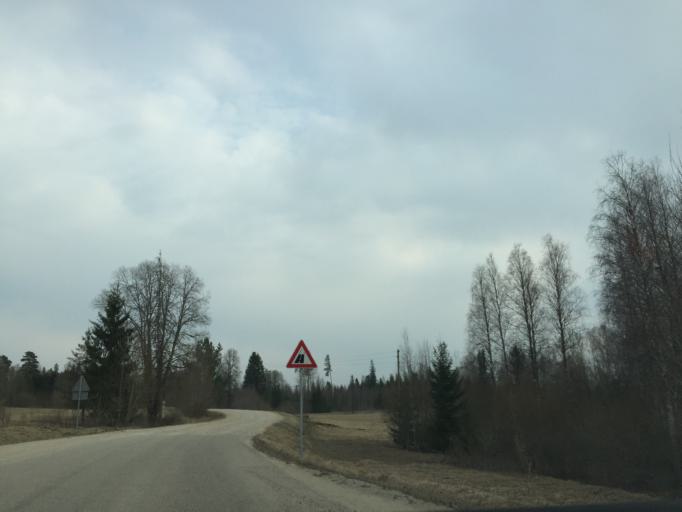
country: LV
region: Priekuli
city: Priekuli
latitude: 57.2117
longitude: 25.4136
